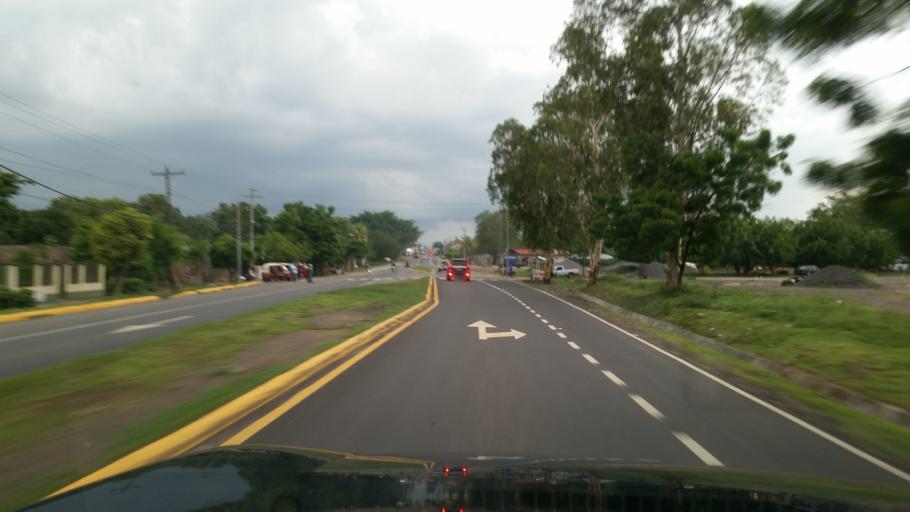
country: NI
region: Leon
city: Nagarote
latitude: 12.2723
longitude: -86.5636
